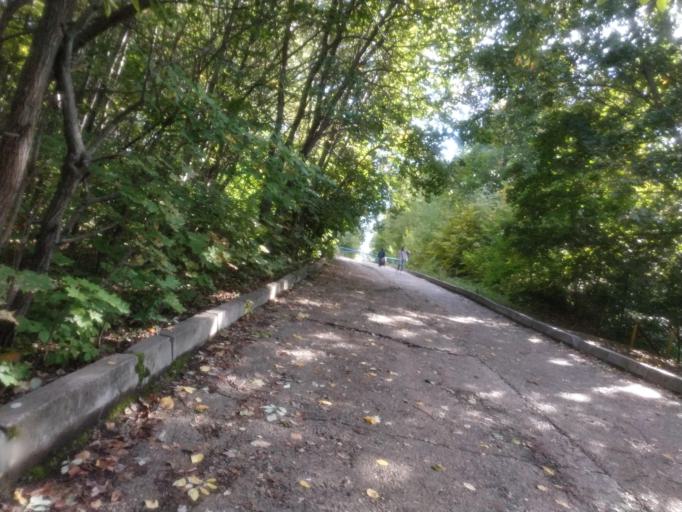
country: RU
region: Chuvashia
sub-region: Cheboksarskiy Rayon
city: Cheboksary
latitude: 56.1541
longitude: 47.1649
